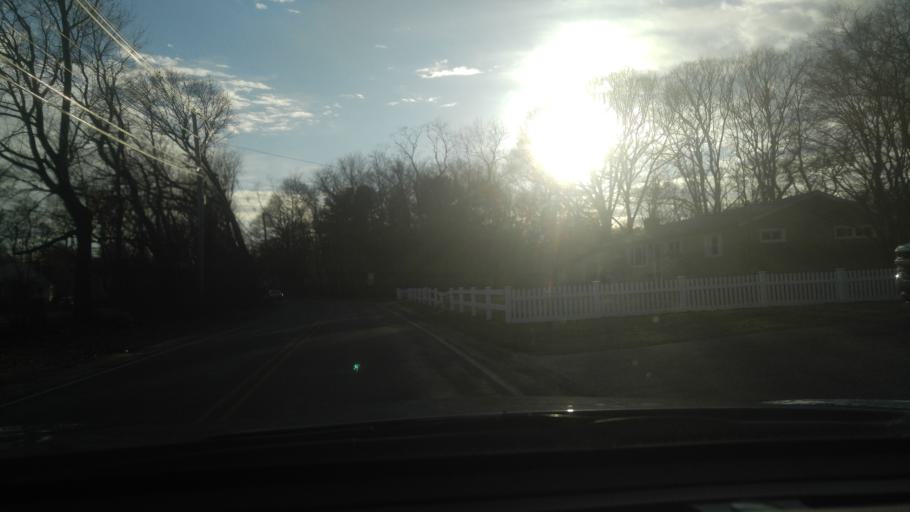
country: US
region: Rhode Island
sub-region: Washington County
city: North Kingstown
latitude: 41.5957
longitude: -71.4885
